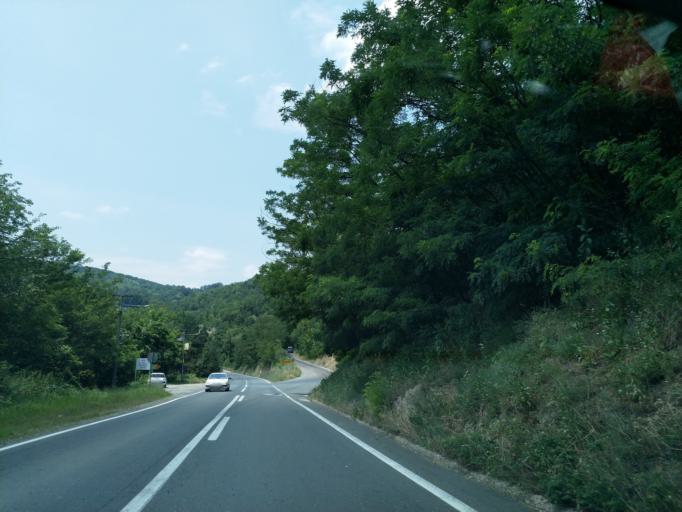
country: RS
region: Central Serbia
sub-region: Rasinski Okrug
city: Aleksandrovac
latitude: 43.4130
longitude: 21.1634
